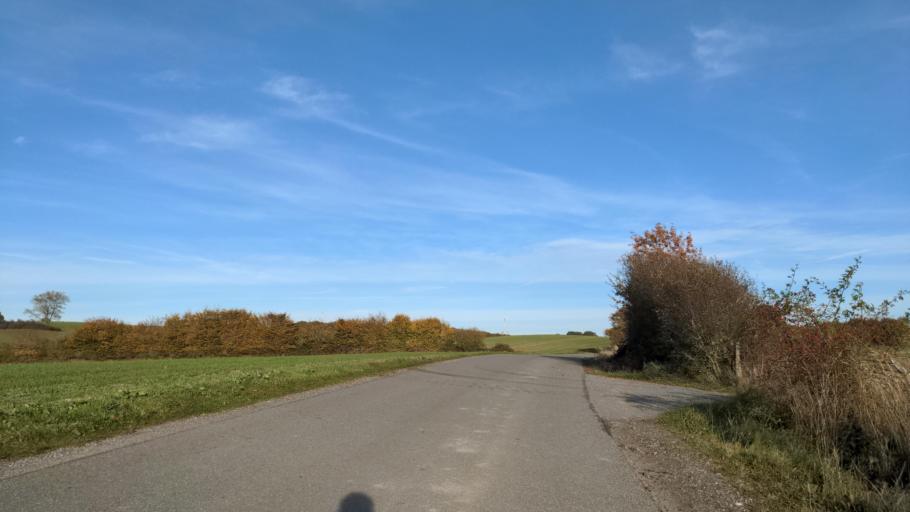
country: DE
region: Schleswig-Holstein
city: Kirchnuchel
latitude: 54.1928
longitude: 10.6807
